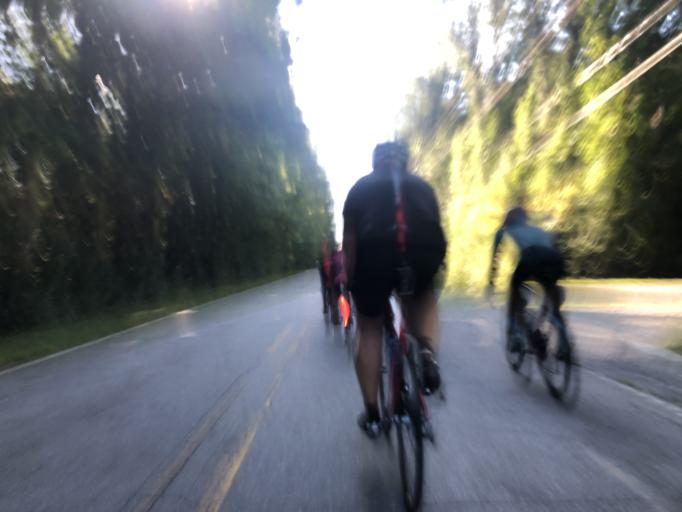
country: US
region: Georgia
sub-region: Fulton County
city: Chattahoochee Hills
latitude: 33.5495
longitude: -84.7642
